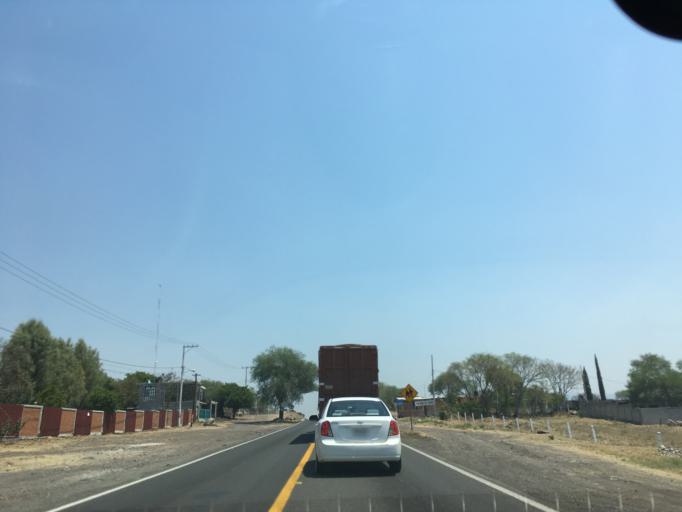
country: MX
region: Michoacan
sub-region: Cuitzeo
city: Cuamio
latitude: 20.0277
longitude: -101.1531
